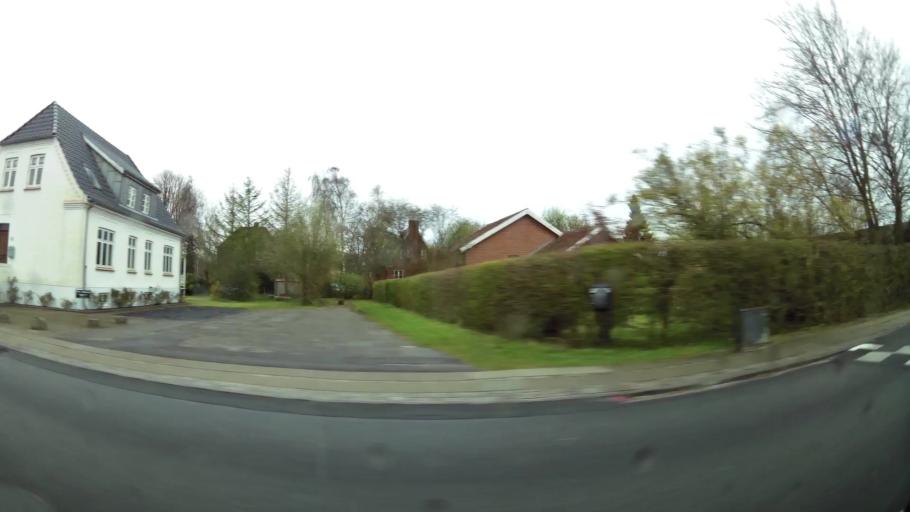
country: DK
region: Central Jutland
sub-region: Holstebro Kommune
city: Holstebro
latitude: 56.3640
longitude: 8.6275
